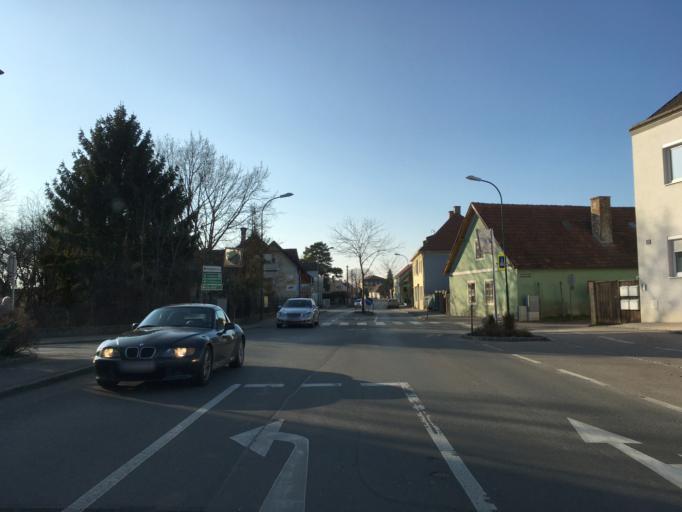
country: AT
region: Lower Austria
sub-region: Politischer Bezirk Tulln
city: Konigstetten
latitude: 48.3324
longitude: 16.1206
